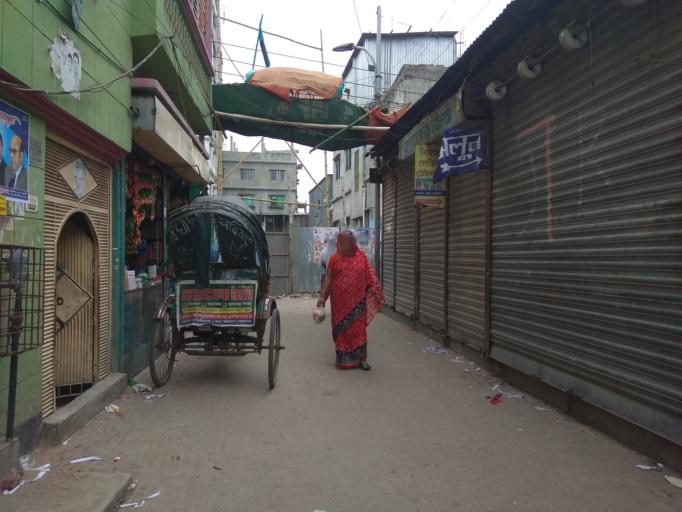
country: BD
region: Dhaka
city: Azimpur
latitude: 23.7213
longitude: 90.3744
